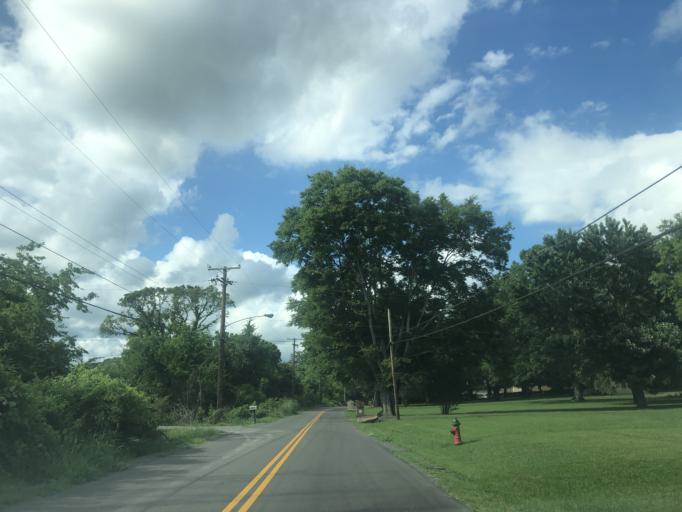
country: US
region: Tennessee
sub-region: Davidson County
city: Nashville
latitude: 36.2237
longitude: -86.8521
